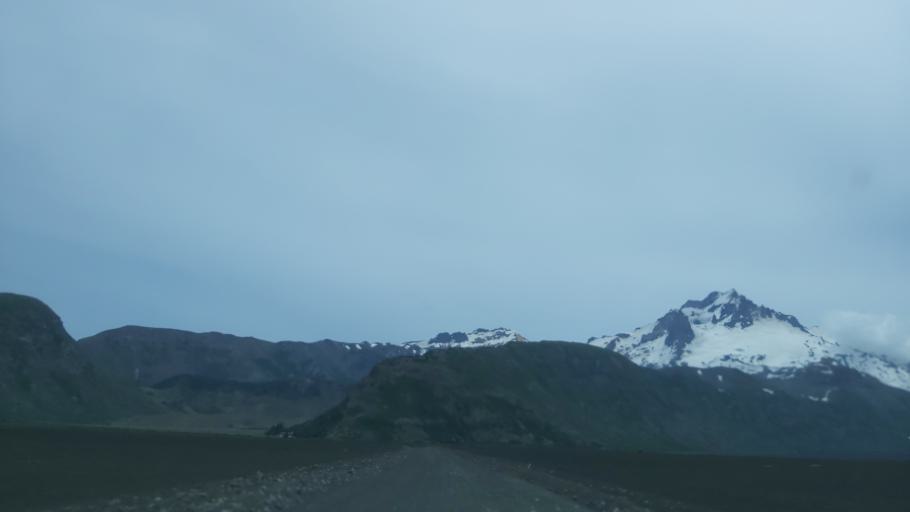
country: AR
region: Neuquen
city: Andacollo
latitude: -37.4599
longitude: -71.3059
